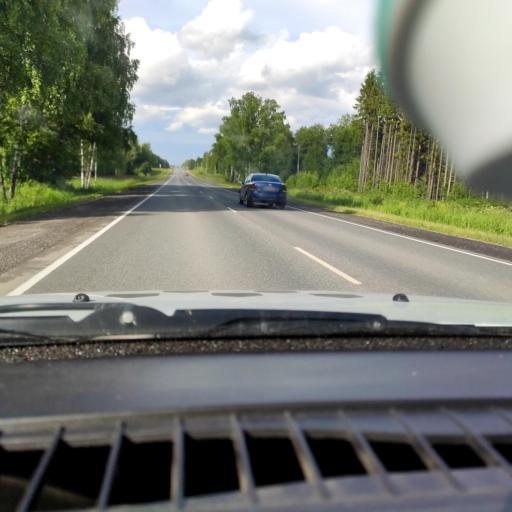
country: RU
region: Perm
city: Orda
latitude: 57.2530
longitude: 57.0017
